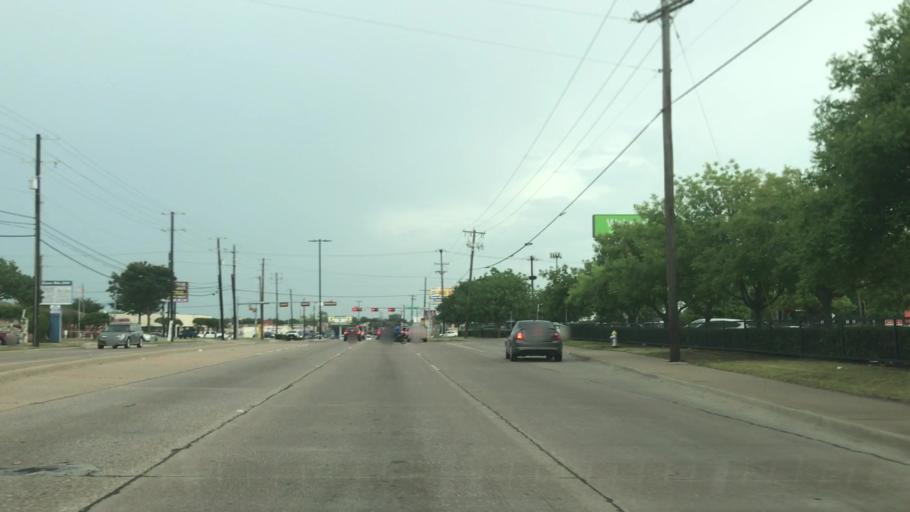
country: US
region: Texas
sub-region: Dallas County
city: Garland
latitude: 32.8659
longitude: -96.6068
